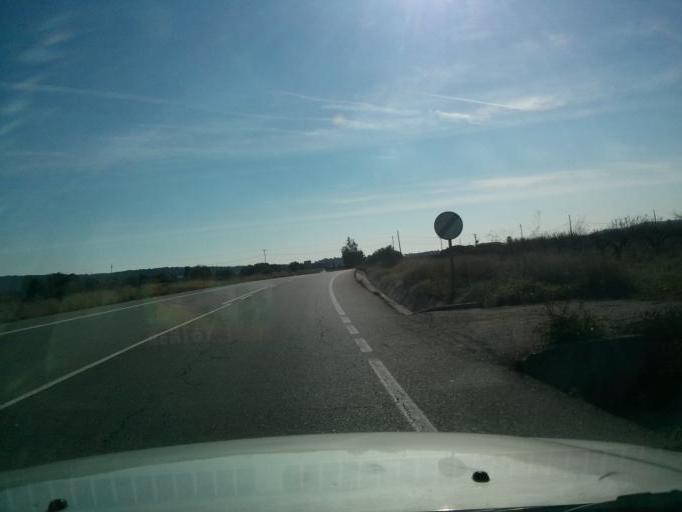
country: ES
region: Catalonia
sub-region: Provincia de Tarragona
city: Santa Oliva
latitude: 41.2467
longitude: 1.5454
